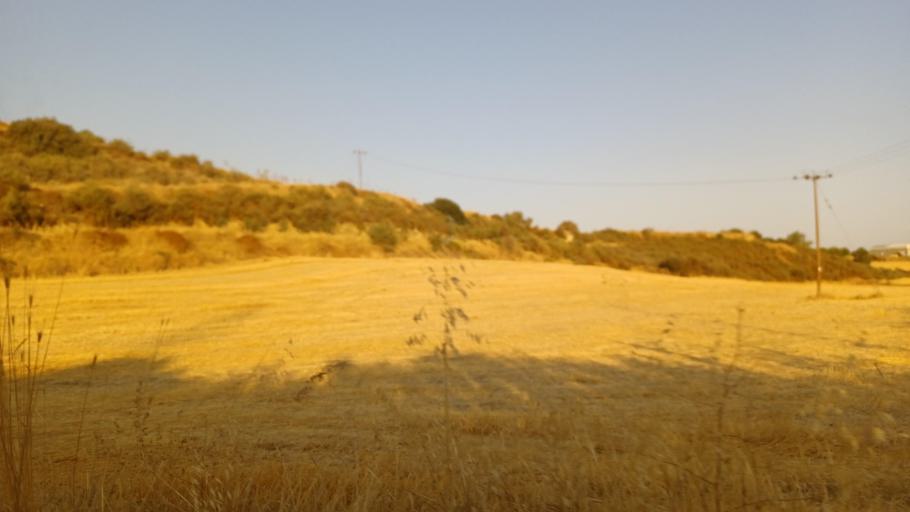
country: CY
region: Pafos
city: Polis
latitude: 35.0443
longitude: 32.4622
